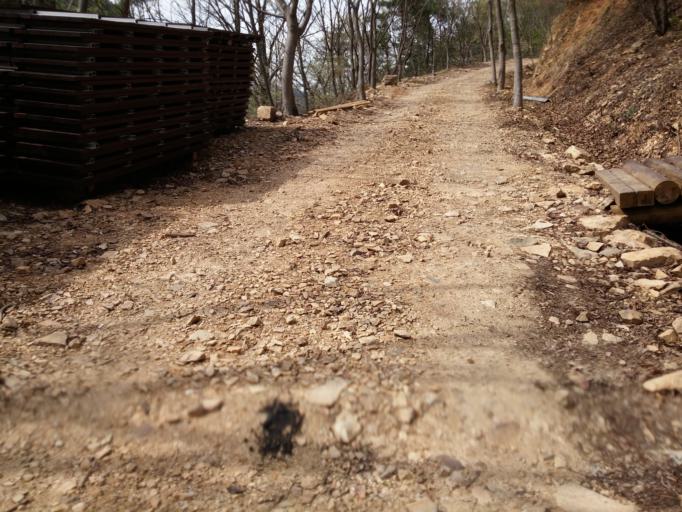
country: KR
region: Chungcheongbuk-do
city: Okcheon
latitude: 36.2416
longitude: 127.5563
